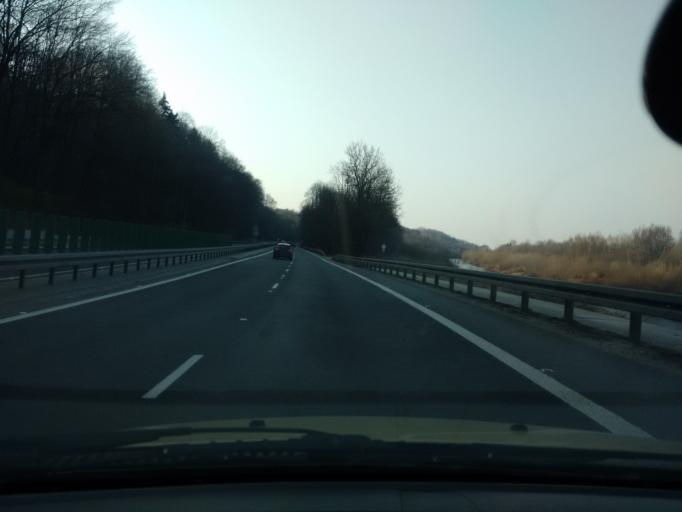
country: PL
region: Silesian Voivodeship
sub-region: Powiat cieszynski
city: Skoczow
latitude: 49.8220
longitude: 18.7924
